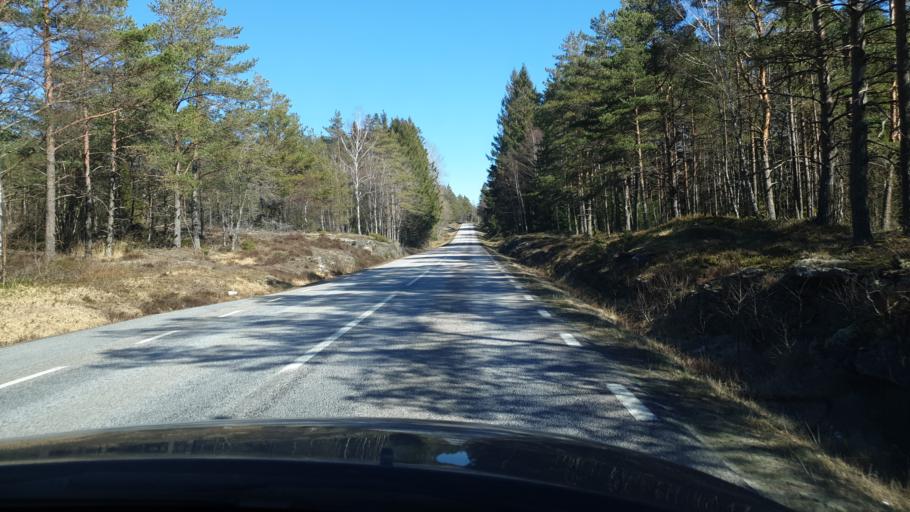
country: SE
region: Vaestra Goetaland
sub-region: Tanums Kommun
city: Tanumshede
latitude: 58.7390
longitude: 11.4503
